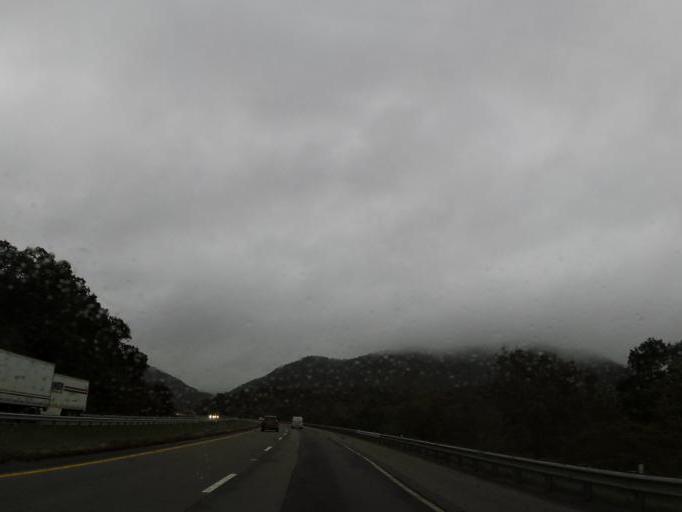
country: US
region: Virginia
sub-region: Wythe County
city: Wytheville
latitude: 37.0061
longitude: -81.0994
